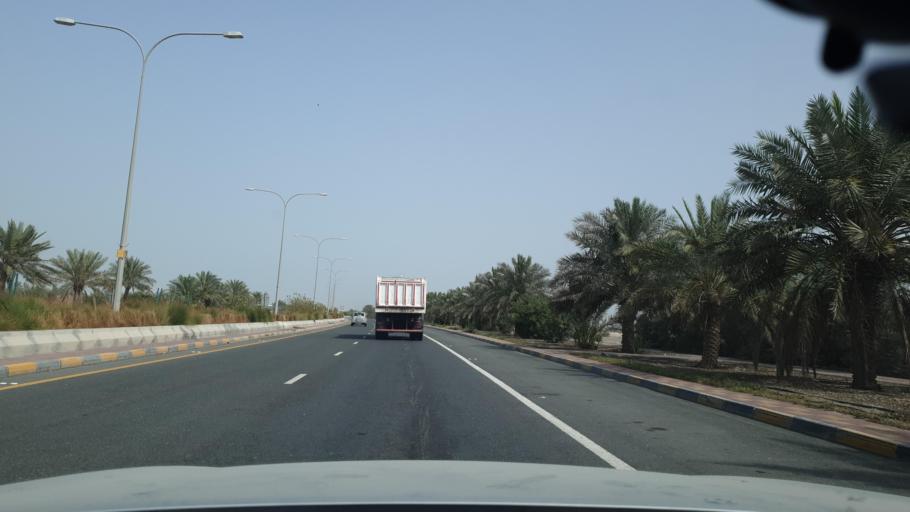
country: QA
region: Al Wakrah
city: Umm Sa'id
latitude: 25.0124
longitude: 51.5547
